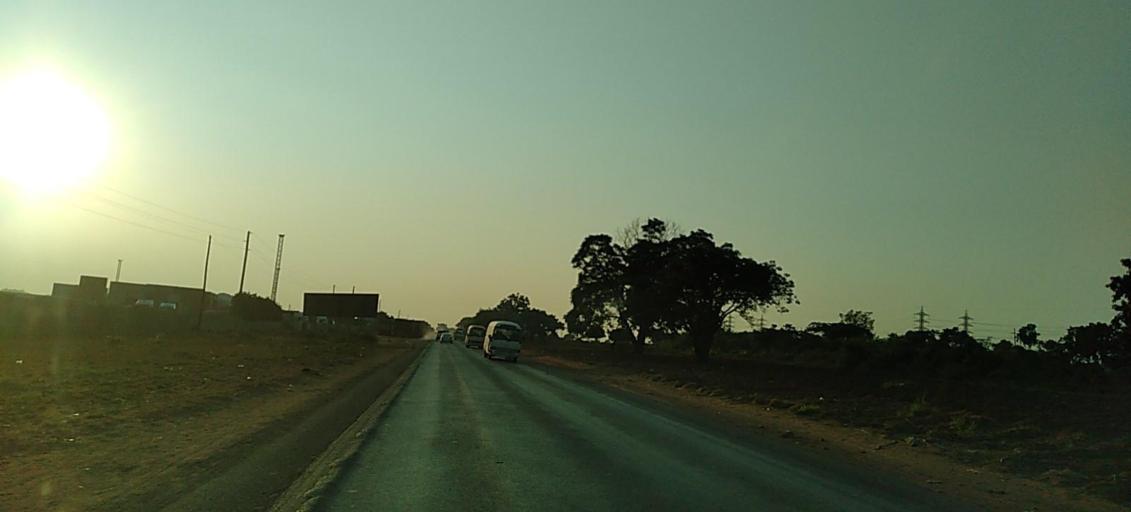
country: ZM
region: Copperbelt
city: Ndola
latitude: -13.0250
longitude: 28.6762
